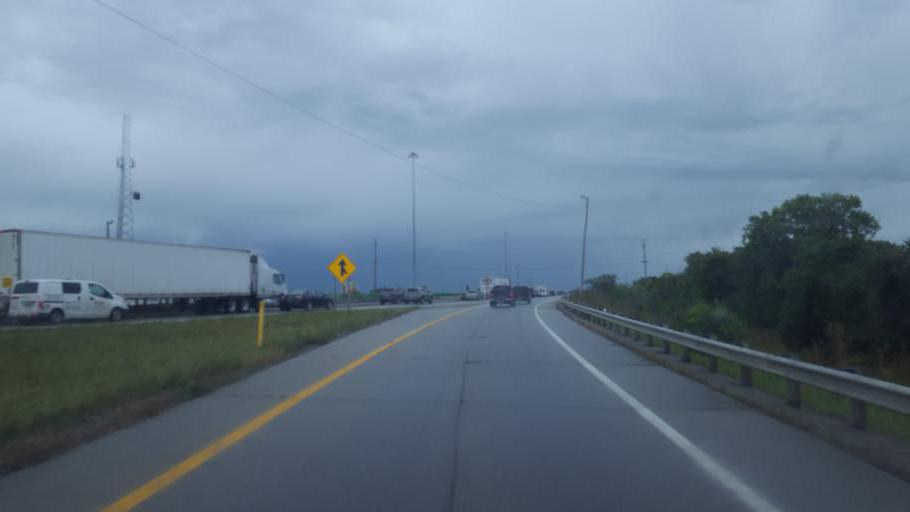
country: US
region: Ohio
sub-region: Cuyahoga County
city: North Randall
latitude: 41.4265
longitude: -81.5084
